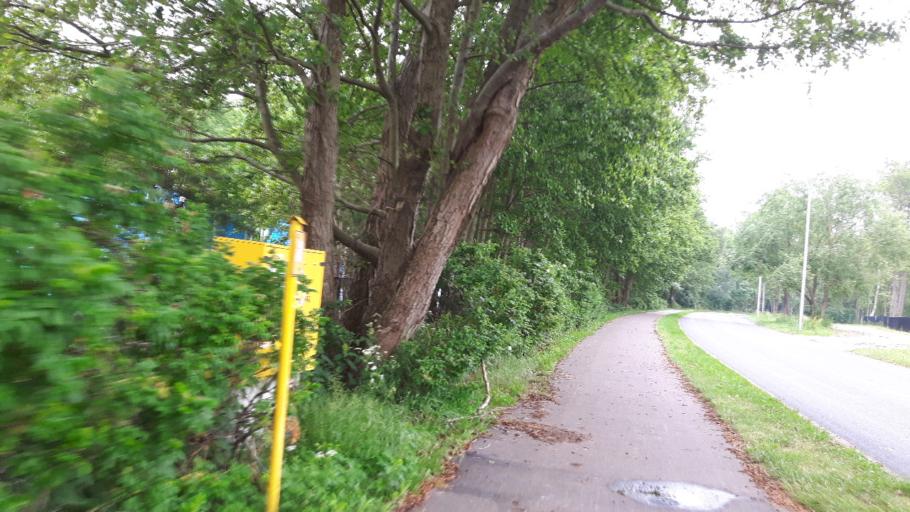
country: PL
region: West Pomeranian Voivodeship
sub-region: Powiat koszalinski
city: Mielno
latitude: 54.2698
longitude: 16.0912
